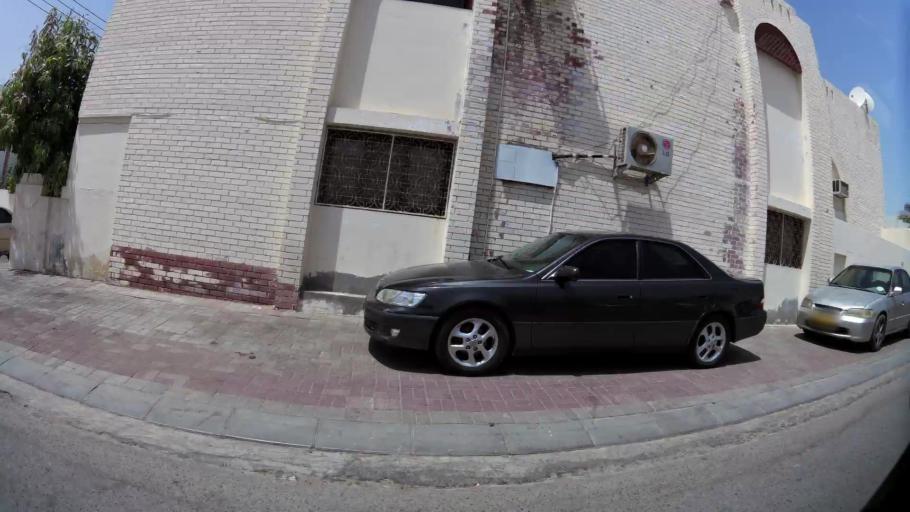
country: OM
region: Muhafazat Masqat
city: Bawshar
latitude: 23.5900
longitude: 58.4346
